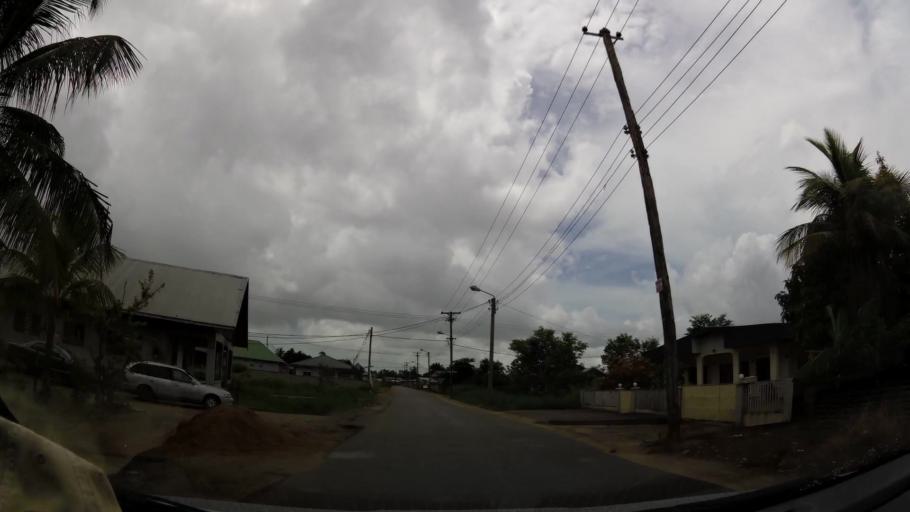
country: SR
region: Wanica
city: Lelydorp
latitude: 5.7886
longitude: -55.2224
